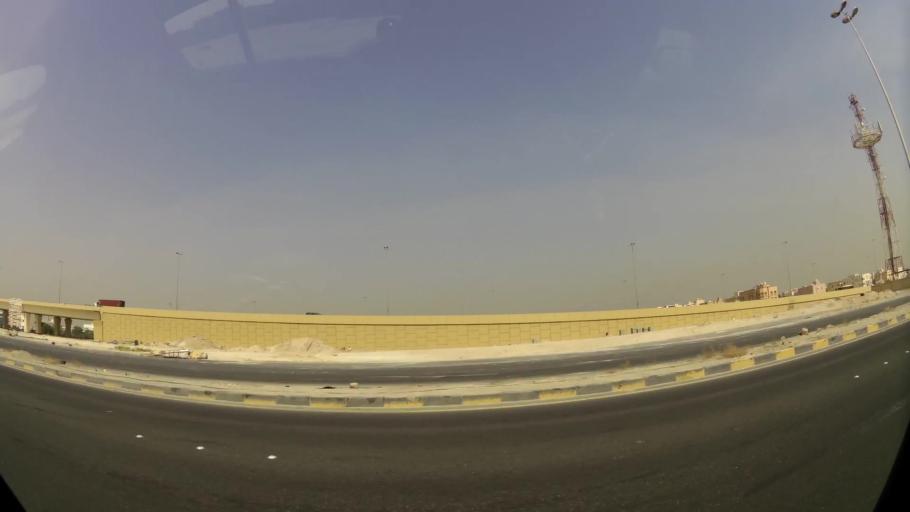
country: KW
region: Al Asimah
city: Ar Rabiyah
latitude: 29.3096
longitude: 47.8677
